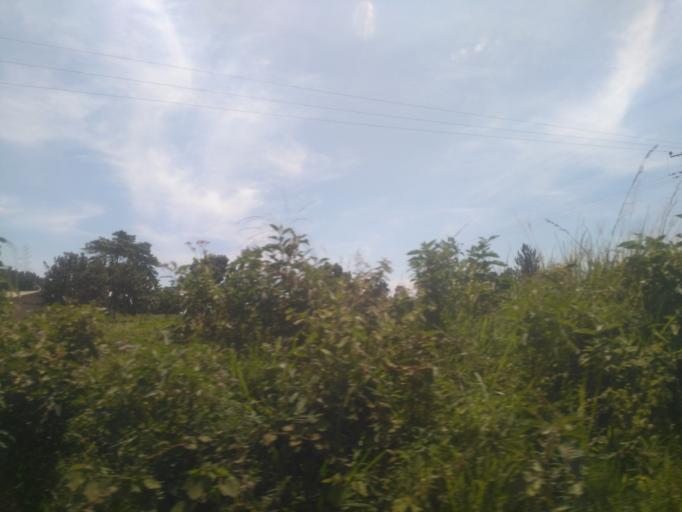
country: UG
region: Central Region
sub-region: Wakiso District
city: Entebbe
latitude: 0.0387
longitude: 32.4258
